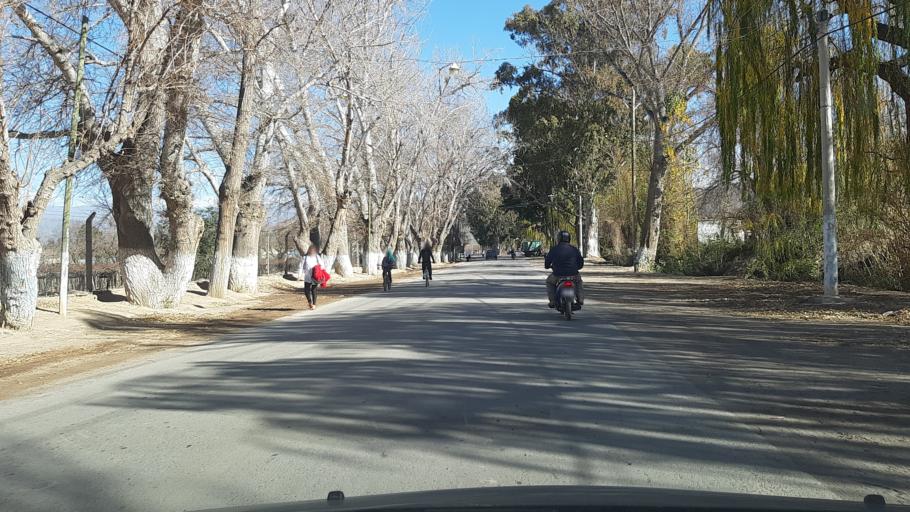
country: AR
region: San Juan
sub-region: Departamento de Zonda
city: Zonda
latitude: -31.4613
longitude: -68.7339
